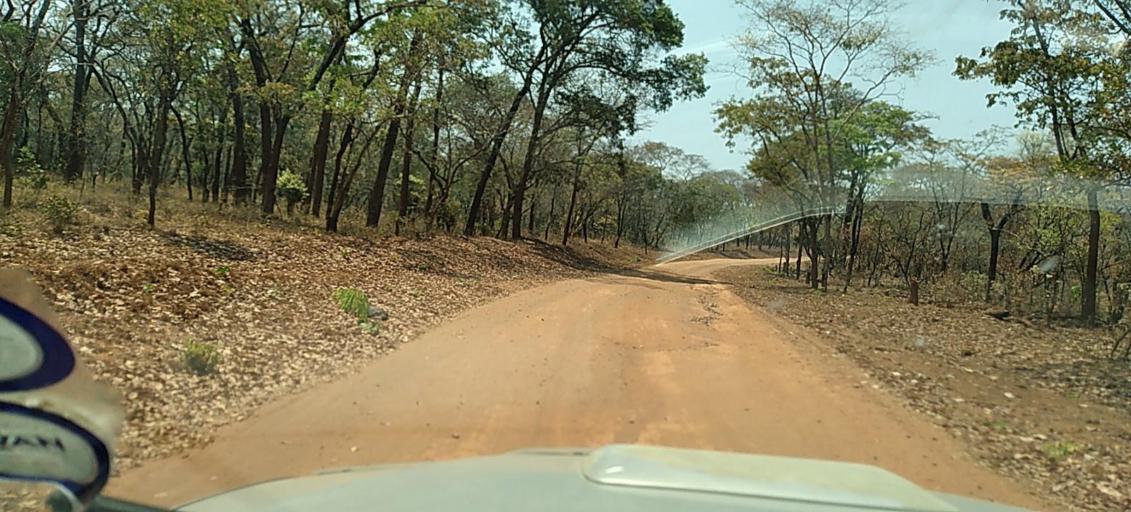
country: ZM
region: North-Western
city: Kasempa
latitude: -13.5485
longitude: 26.0592
